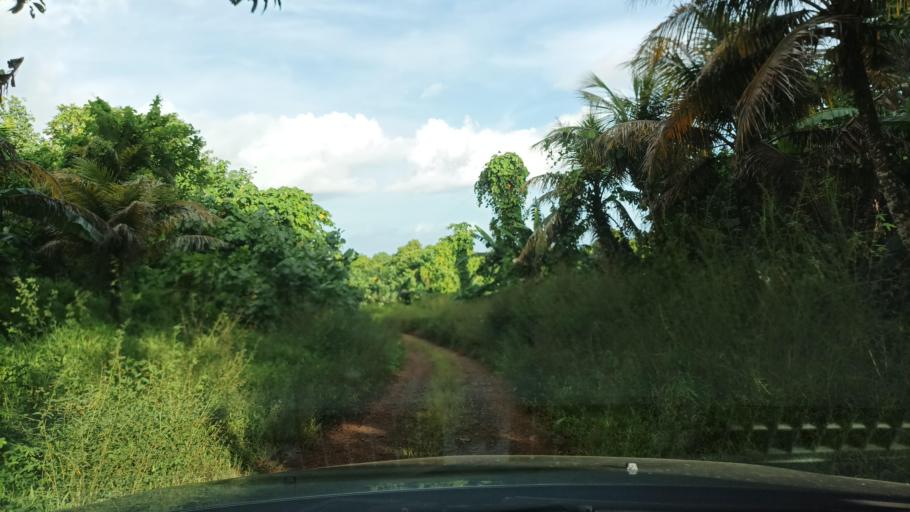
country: FM
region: Kosrae
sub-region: Utwe Municipality
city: Utwe
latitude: 5.2742
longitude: 162.9455
